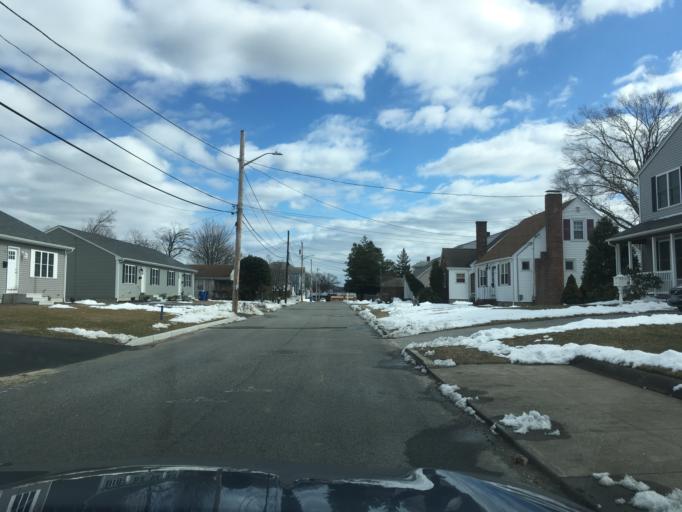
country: US
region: Rhode Island
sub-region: Providence County
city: Cranston
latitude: 41.7873
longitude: -71.4371
